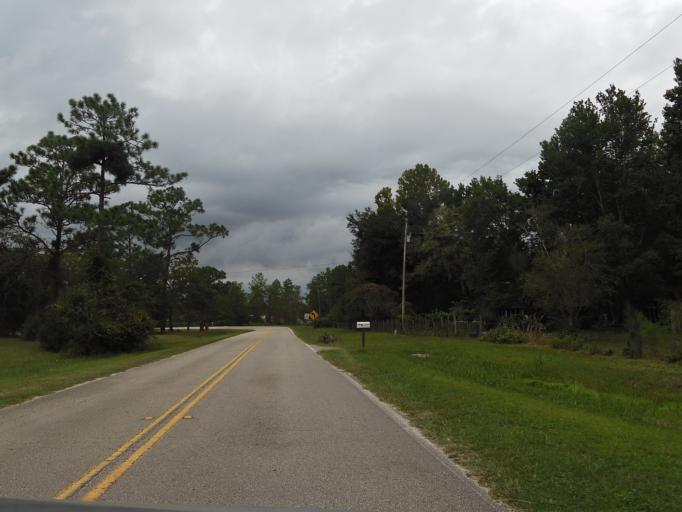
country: US
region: Florida
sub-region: Clay County
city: Middleburg
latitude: 30.1274
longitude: -81.9631
